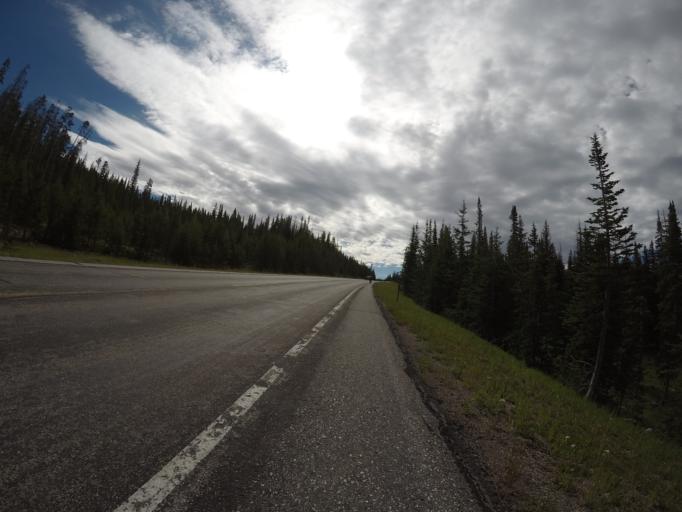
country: US
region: Wyoming
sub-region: Carbon County
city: Saratoga
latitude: 41.3250
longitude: -106.4255
